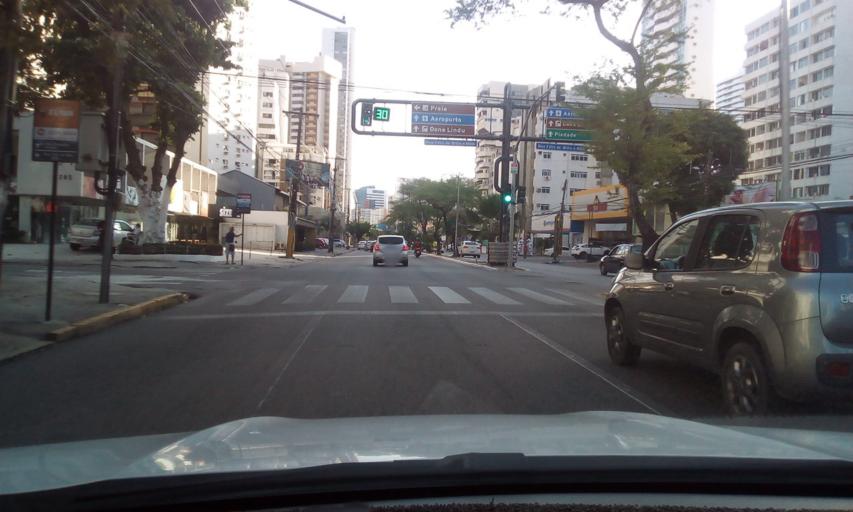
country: BR
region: Pernambuco
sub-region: Recife
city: Recife
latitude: -8.1172
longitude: -34.8963
